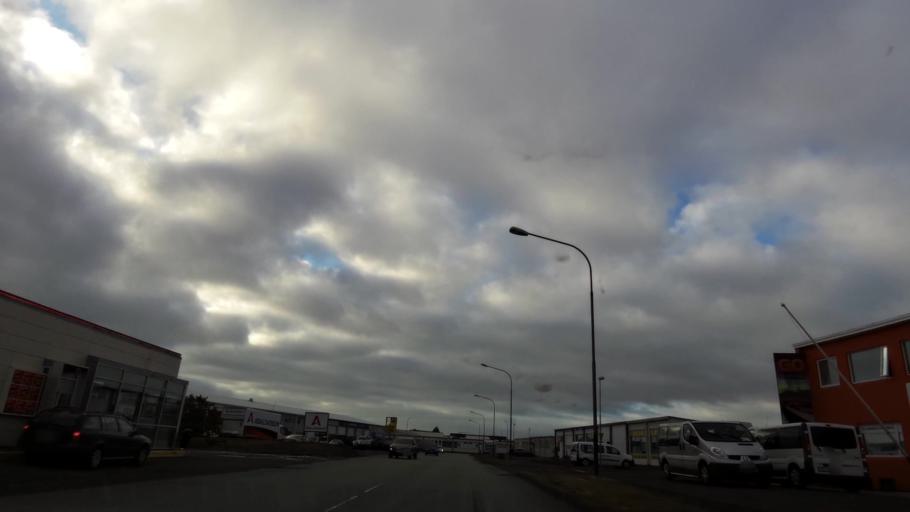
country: IS
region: Capital Region
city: Hafnarfjoerdur
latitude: 64.0763
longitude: -21.9447
